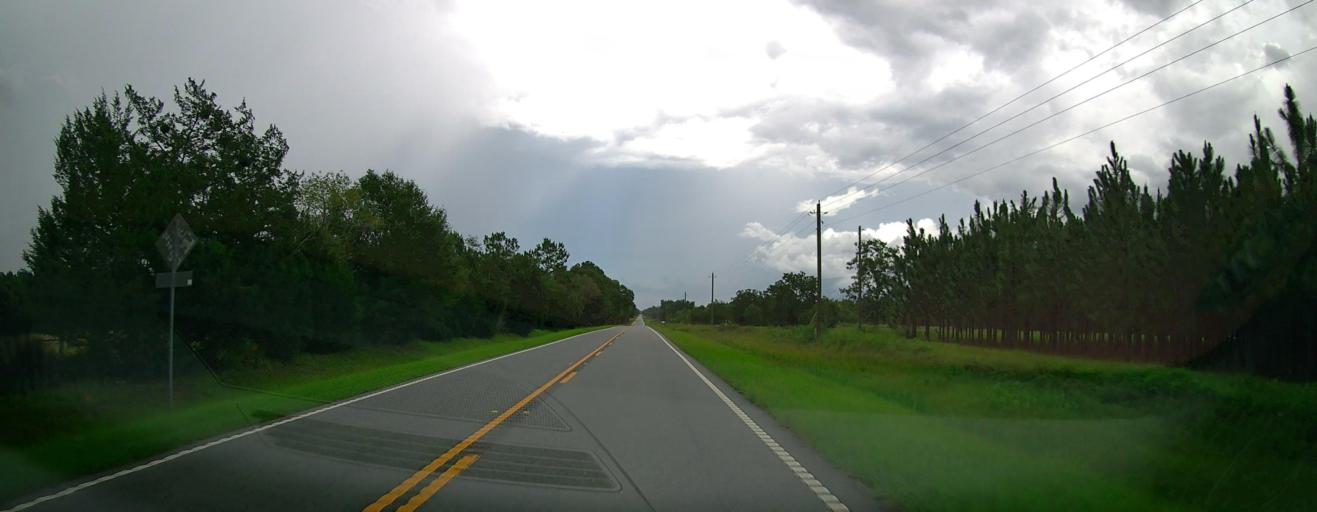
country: US
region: Georgia
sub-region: Pierce County
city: Blackshear
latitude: 31.3707
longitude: -82.1027
